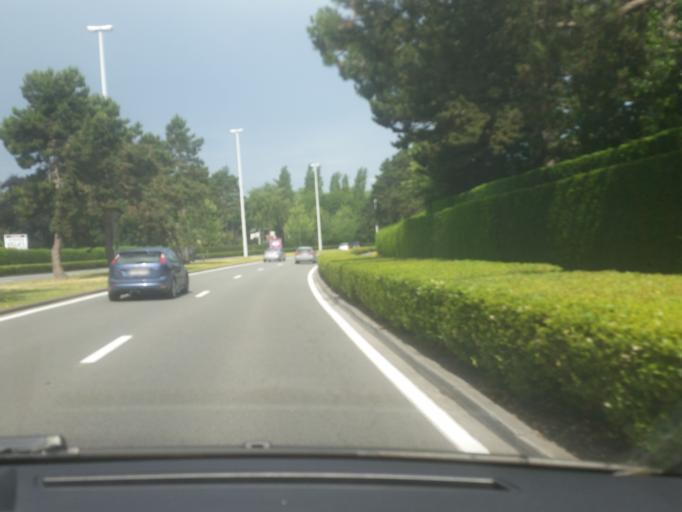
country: BE
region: Flanders
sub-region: Provincie West-Vlaanderen
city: Ostend
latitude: 51.2183
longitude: 2.9209
